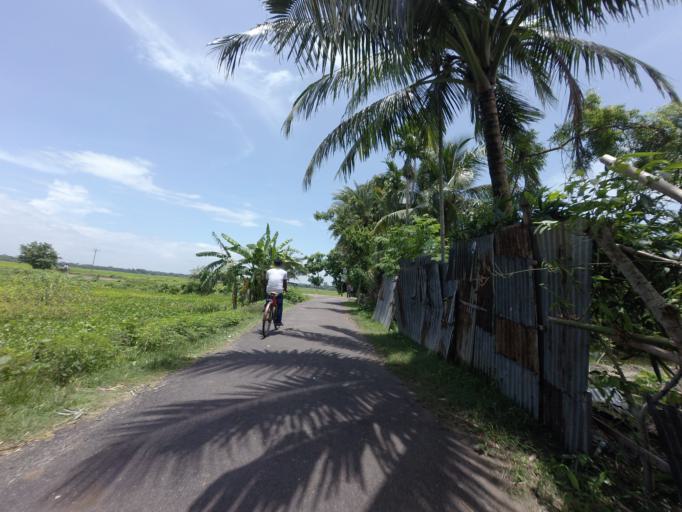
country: BD
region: Khulna
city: Kalia
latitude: 23.0412
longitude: 89.6450
